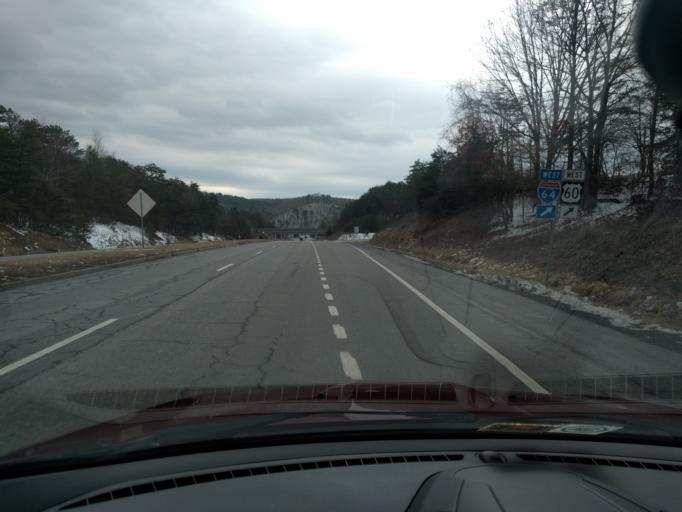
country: US
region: Virginia
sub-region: Alleghany County
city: Clifton Forge
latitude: 37.8352
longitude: -79.7608
